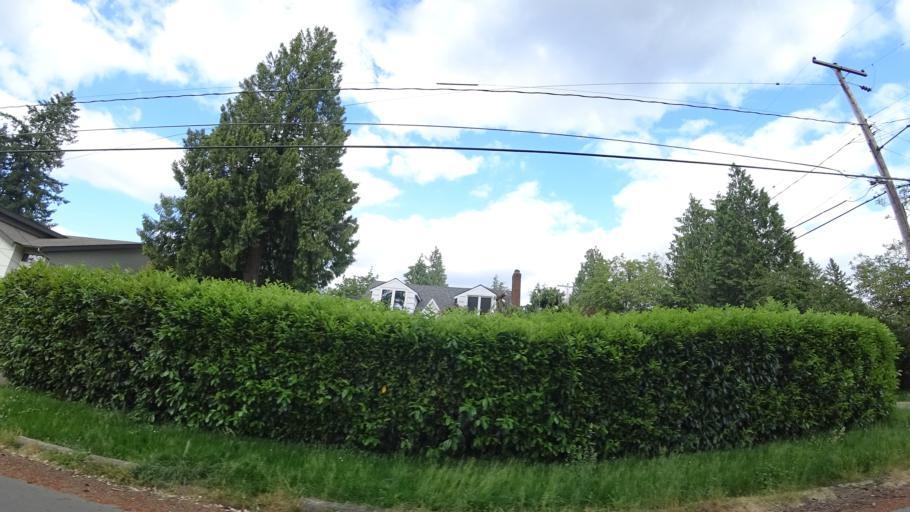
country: US
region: Oregon
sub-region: Washington County
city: Garden Home-Whitford
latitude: 45.4699
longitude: -122.7287
